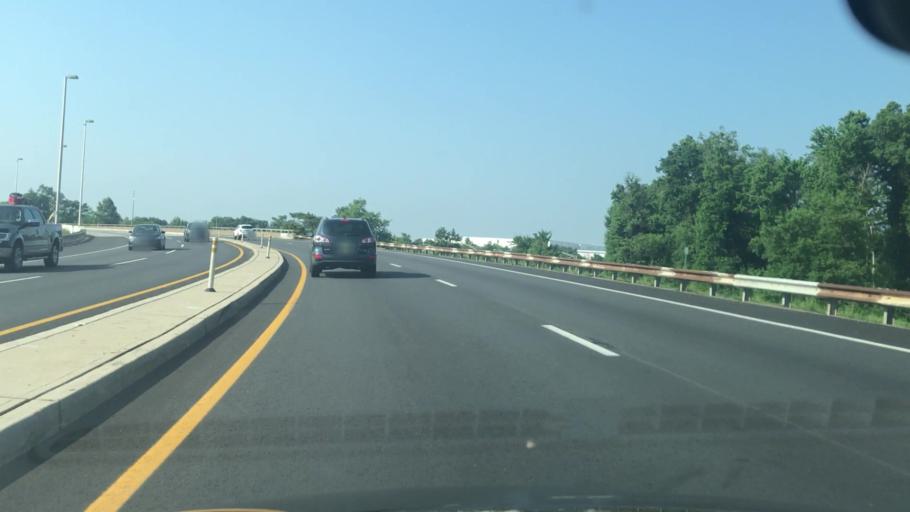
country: US
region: New Jersey
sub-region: Middlesex County
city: Metuchen
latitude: 40.5270
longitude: -74.3430
